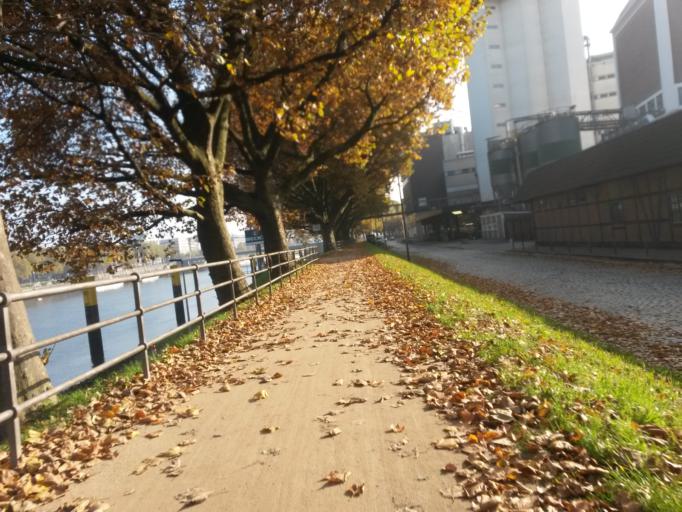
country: DE
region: Bremen
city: Bremen
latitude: 53.0787
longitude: 8.7915
